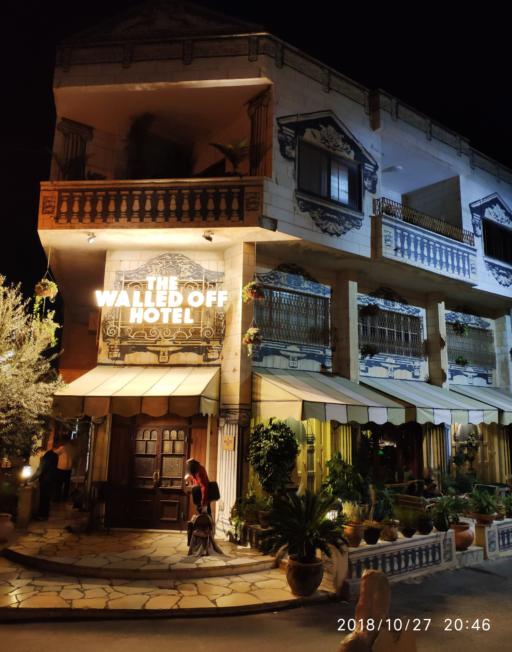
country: PS
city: Khallat Hamamah
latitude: 31.7194
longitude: 35.2035
